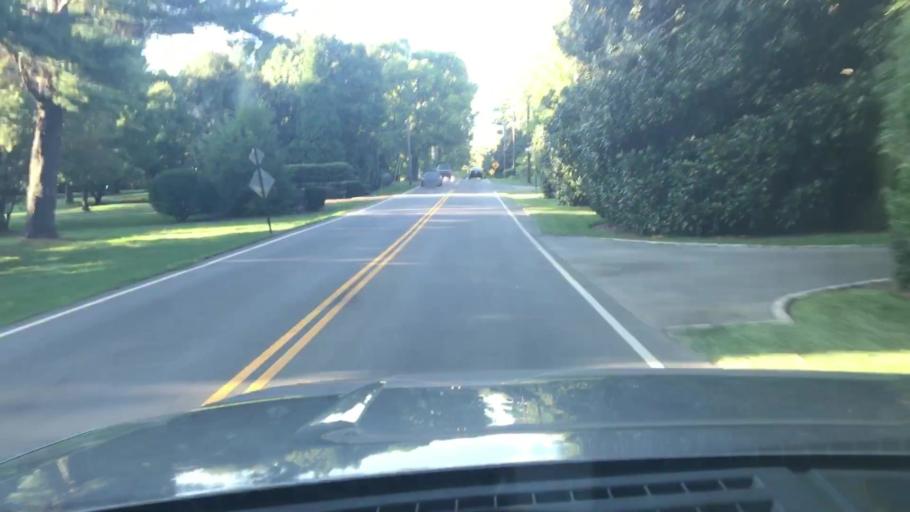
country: US
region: Tennessee
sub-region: Davidson County
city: Belle Meade
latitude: 36.1137
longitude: -86.8481
